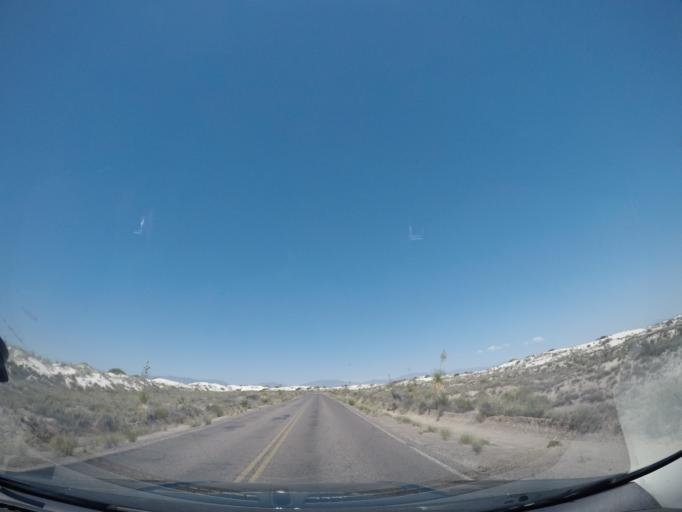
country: US
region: New Mexico
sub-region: Otero County
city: Holloman Air Force Base
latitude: 32.7947
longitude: -106.2305
